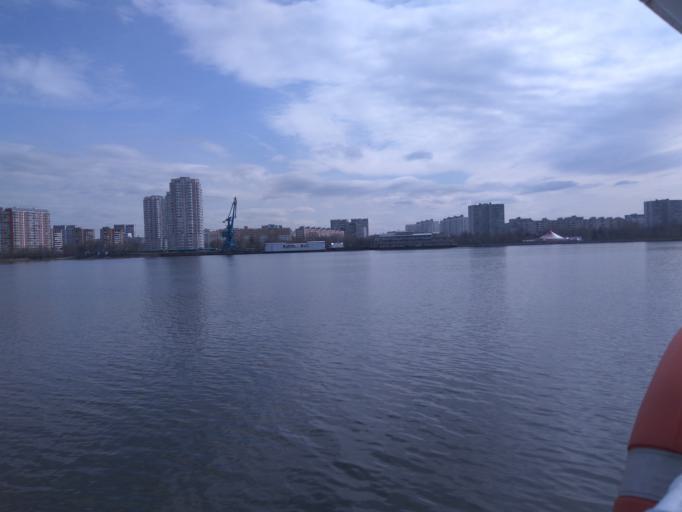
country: RU
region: Moscow
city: Kolomenskoye
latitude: 55.6874
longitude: 37.7082
